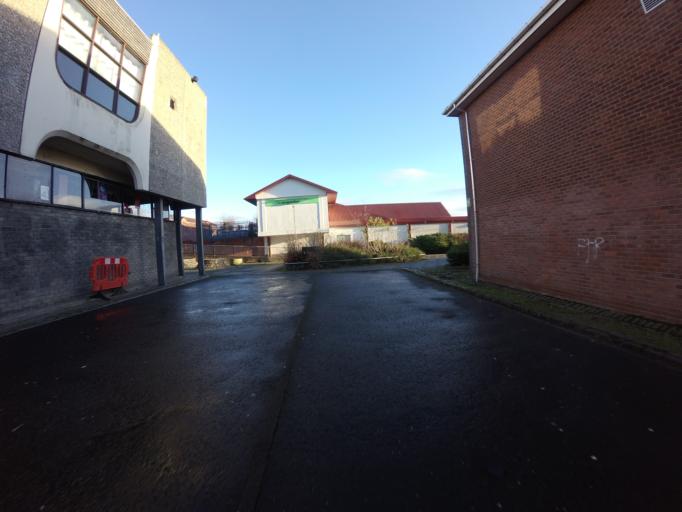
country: GB
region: Scotland
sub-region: West Lothian
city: Mid Calder
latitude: 55.8969
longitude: -3.4974
